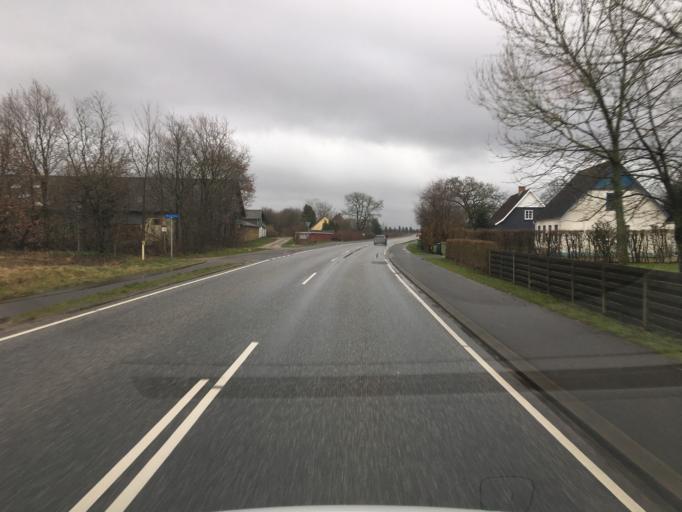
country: DK
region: South Denmark
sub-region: Aabenraa Kommune
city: Tinglev
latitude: 54.9223
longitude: 9.2475
